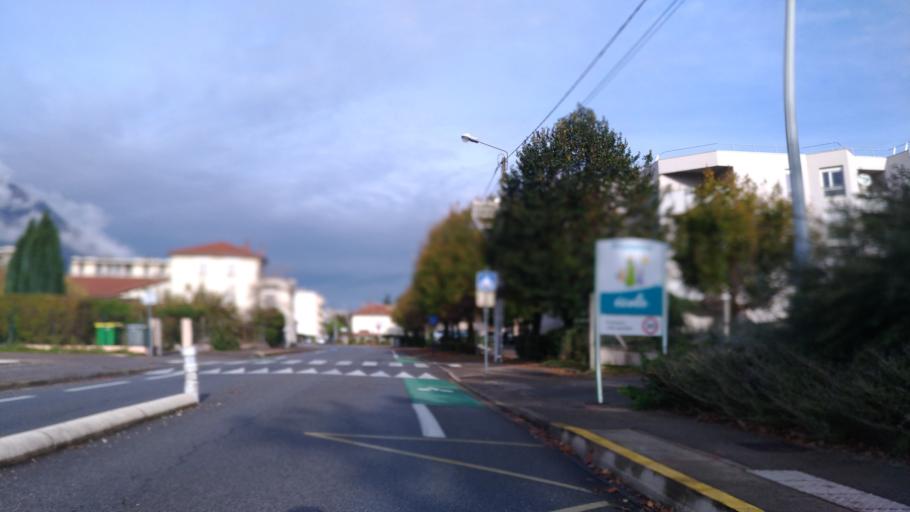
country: FR
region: Rhone-Alpes
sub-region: Departement de l'Isere
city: Fontaine
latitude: 45.1950
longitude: 5.6828
